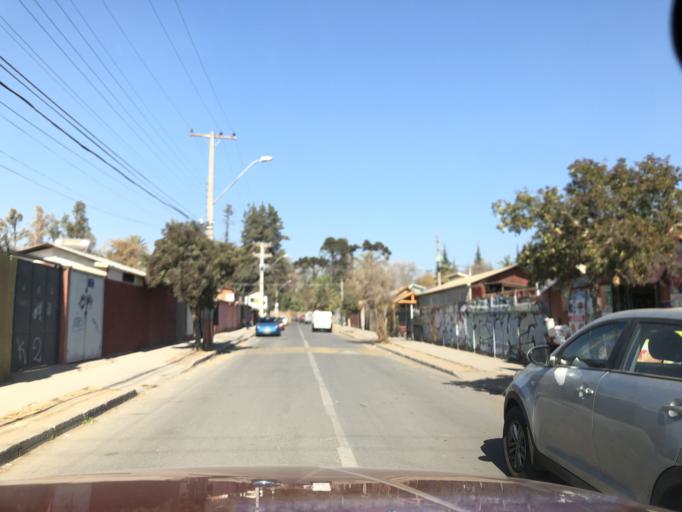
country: CL
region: Santiago Metropolitan
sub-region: Provincia de Cordillera
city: Puente Alto
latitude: -33.5680
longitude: -70.5818
